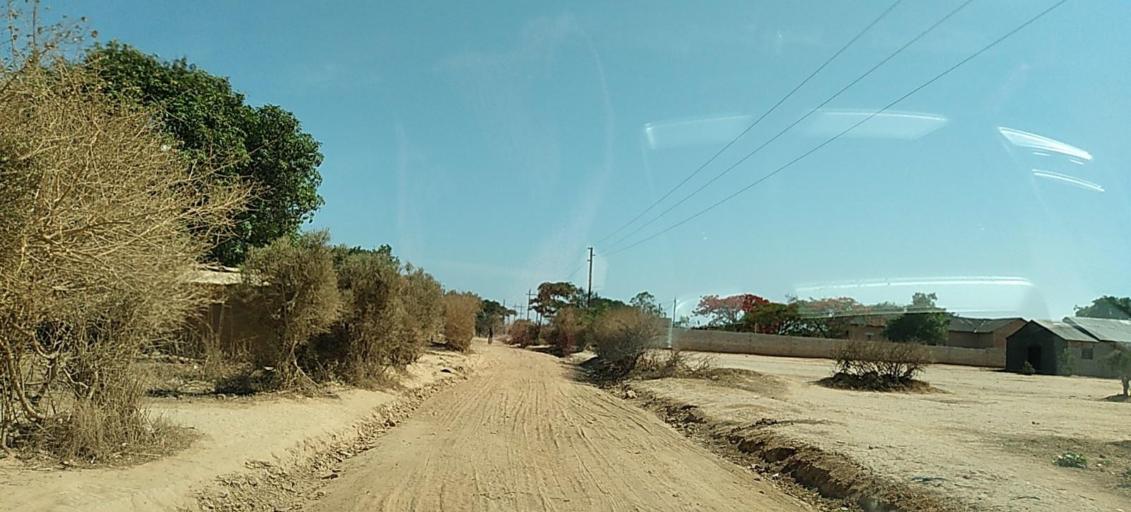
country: ZM
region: Copperbelt
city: Chililabombwe
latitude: -12.3327
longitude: 27.8602
